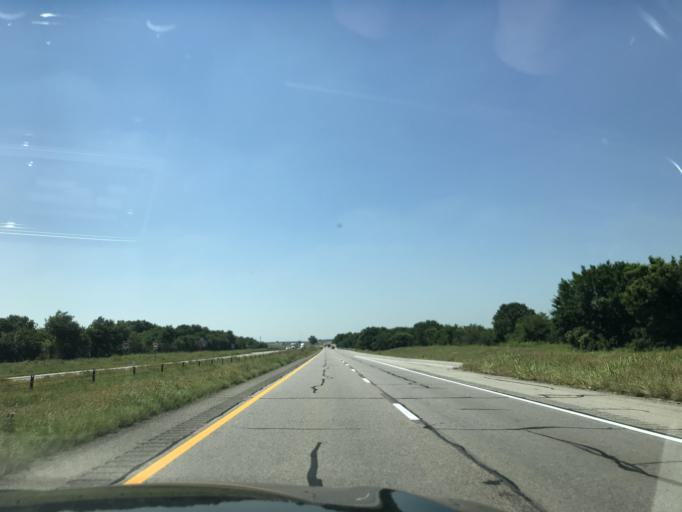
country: US
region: Texas
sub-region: Johnson County
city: Grandview
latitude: 32.2966
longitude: -97.1803
